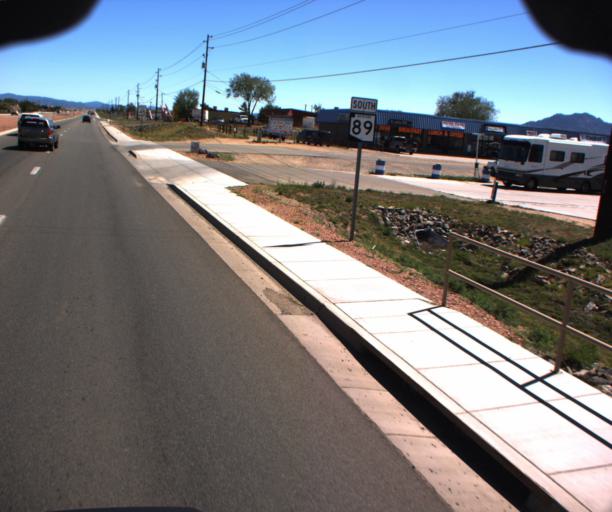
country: US
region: Arizona
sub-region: Yavapai County
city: Chino Valley
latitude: 34.7300
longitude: -112.4542
